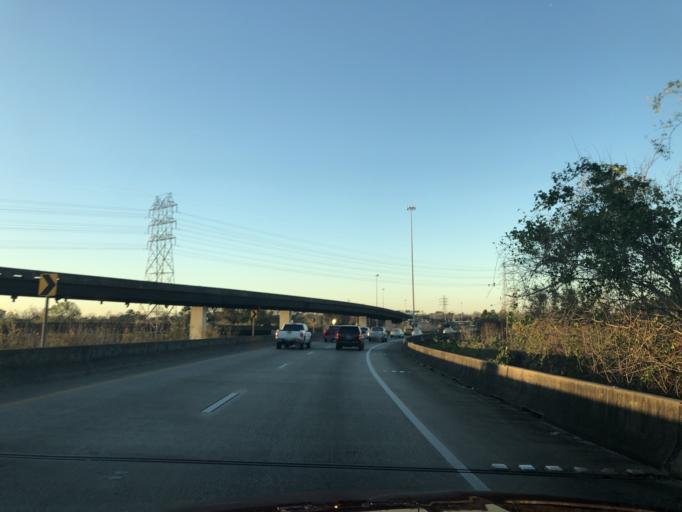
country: US
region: Texas
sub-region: Harris County
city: Houston
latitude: 29.8134
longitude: -95.3507
